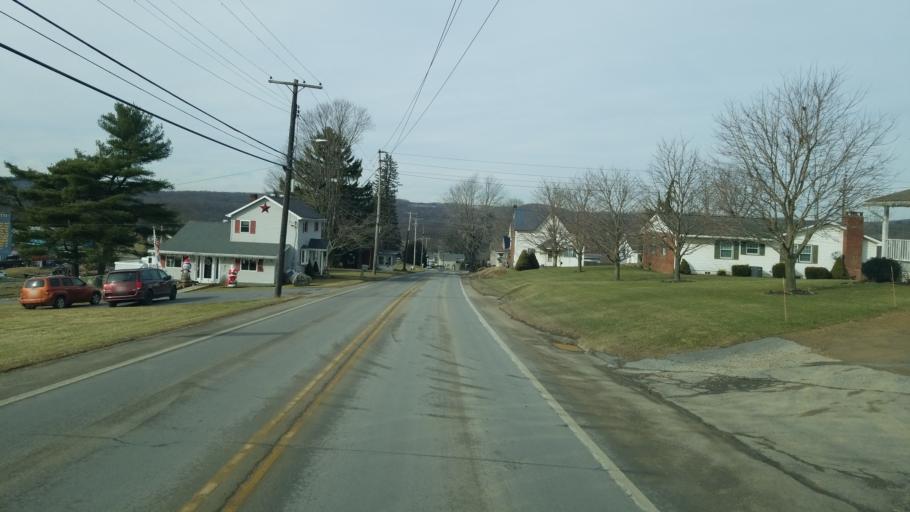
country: US
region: Pennsylvania
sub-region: Jefferson County
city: Punxsutawney
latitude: 40.9363
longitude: -78.9909
